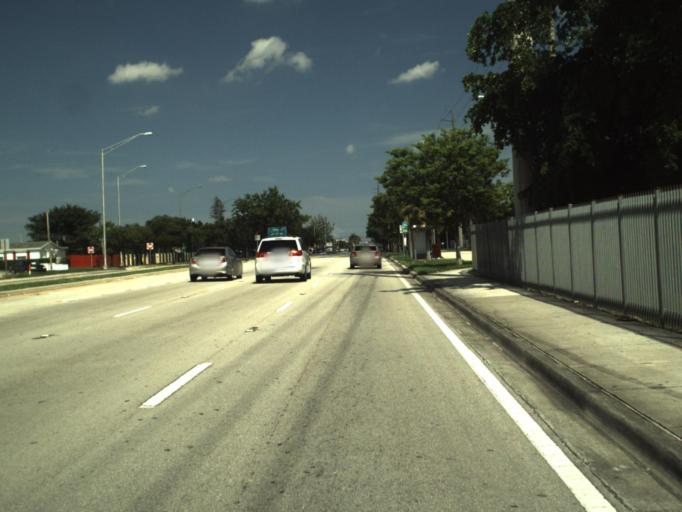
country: US
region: Florida
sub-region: Miami-Dade County
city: Carol City
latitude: 25.9397
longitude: -80.2739
